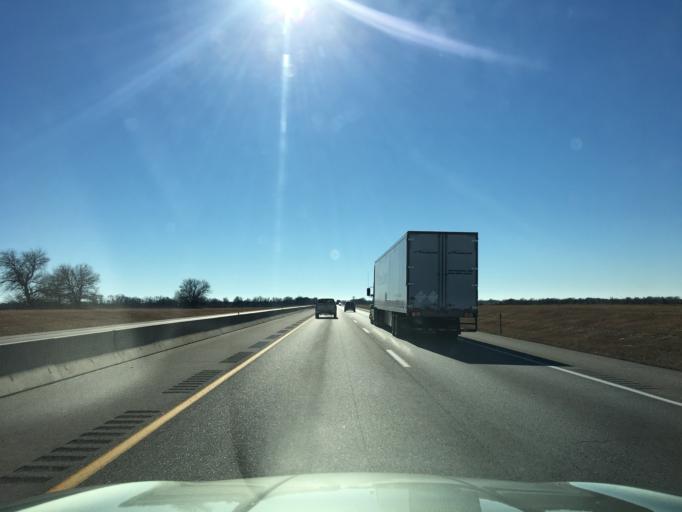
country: US
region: Kansas
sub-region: Sumner County
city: Wellington
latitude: 37.1076
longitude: -97.3388
